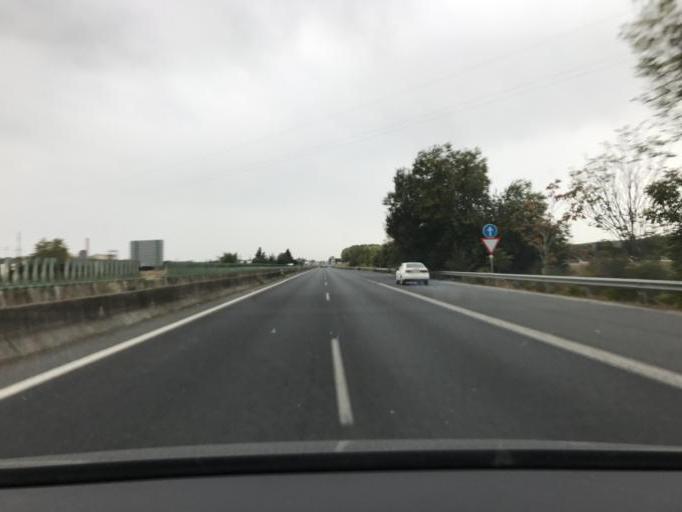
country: ES
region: Andalusia
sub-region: Provincia de Granada
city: Atarfe
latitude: 37.1924
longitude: -3.6708
